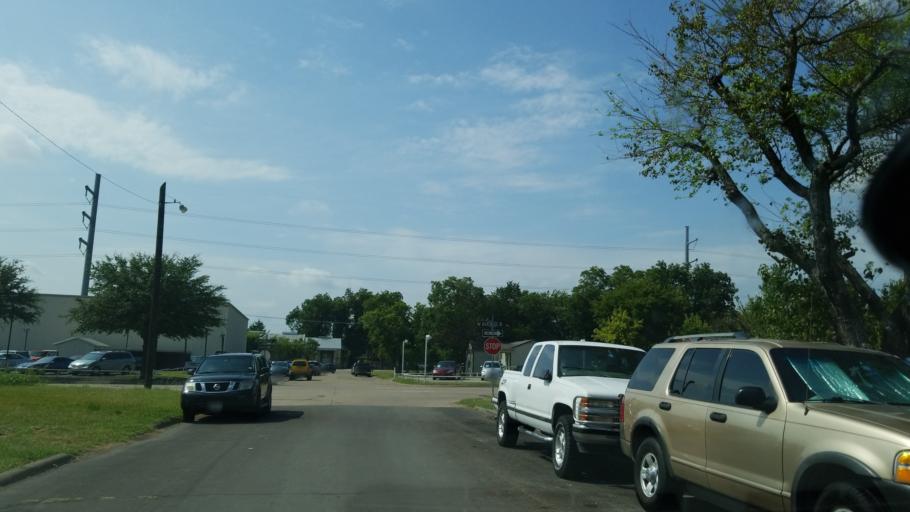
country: US
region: Texas
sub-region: Dallas County
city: Garland
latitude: 32.9112
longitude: -96.6318
